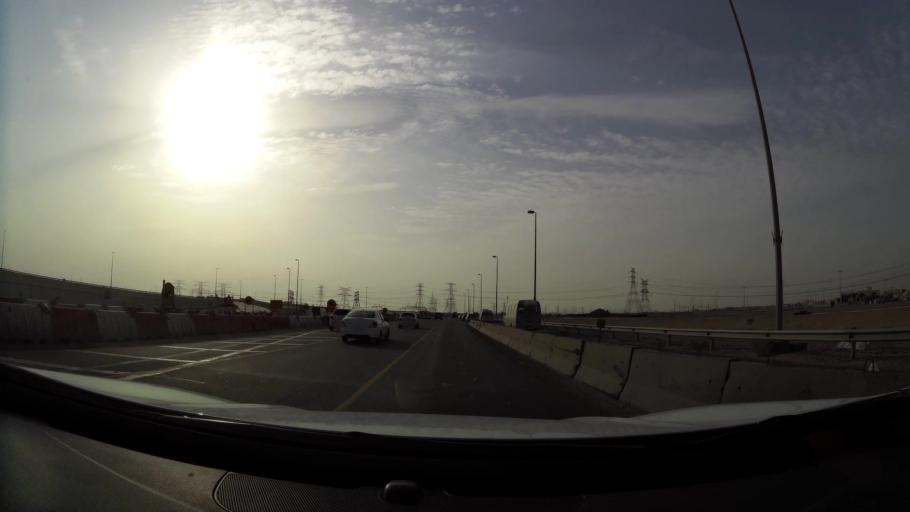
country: AE
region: Abu Dhabi
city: Abu Dhabi
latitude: 24.2935
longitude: 54.5509
